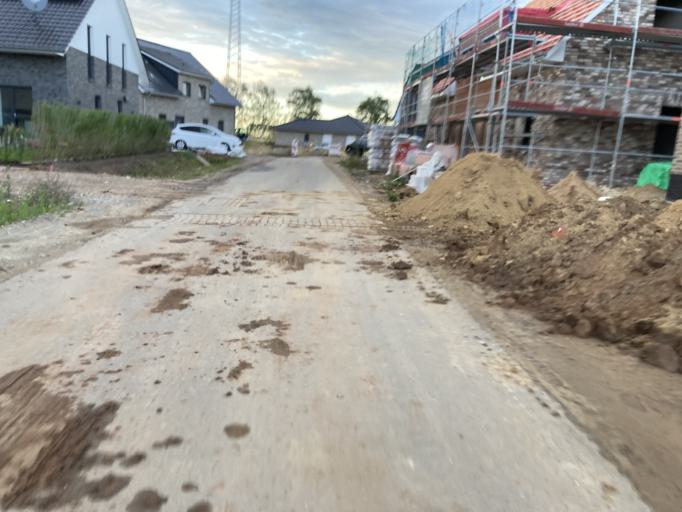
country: DE
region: Lower Saxony
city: Verden
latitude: 52.9264
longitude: 9.2105
